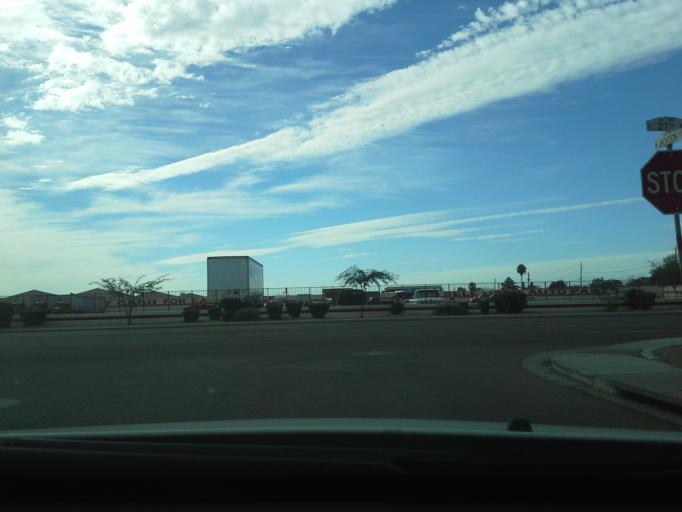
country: US
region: Arizona
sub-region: Maricopa County
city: Phoenix
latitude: 33.4455
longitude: -112.1173
